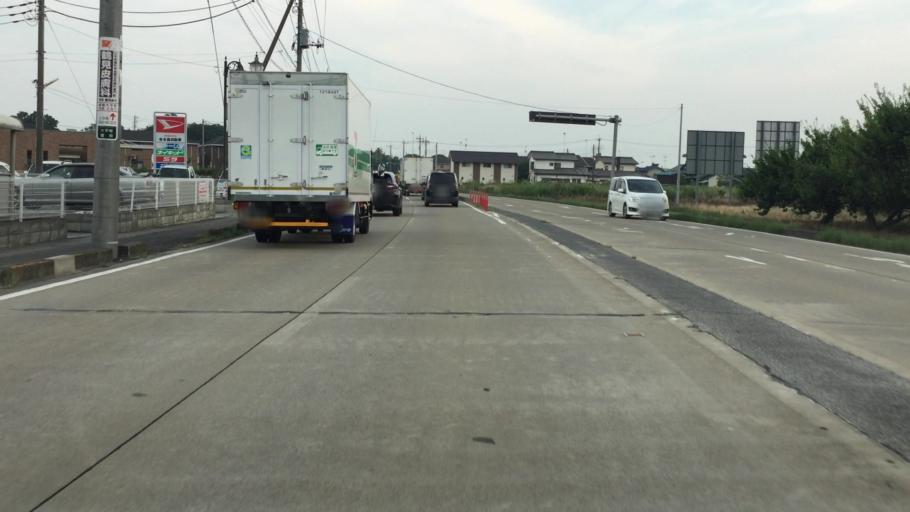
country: JP
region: Tochigi
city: Tochigi
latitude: 36.3420
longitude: 139.6965
